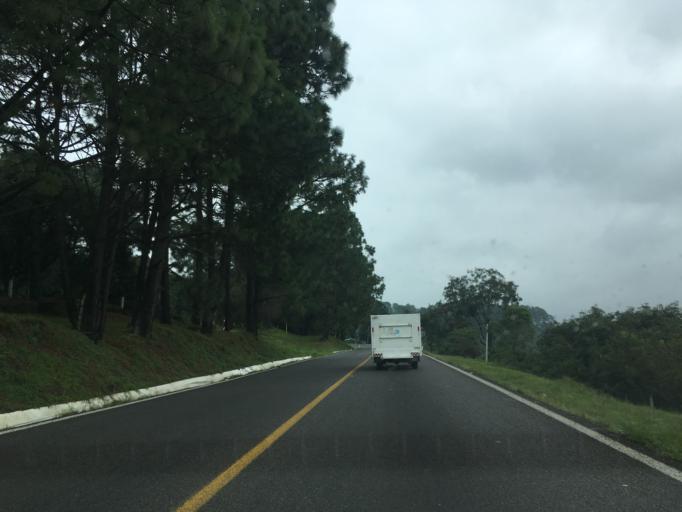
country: MX
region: Michoacan
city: Tingambato
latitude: 19.4853
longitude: -101.8854
